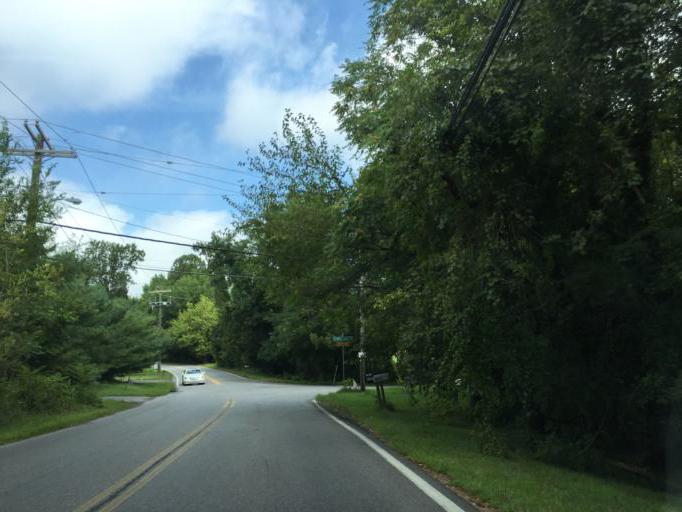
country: US
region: Maryland
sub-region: Anne Arundel County
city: Crownsville
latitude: 39.0136
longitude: -76.5684
